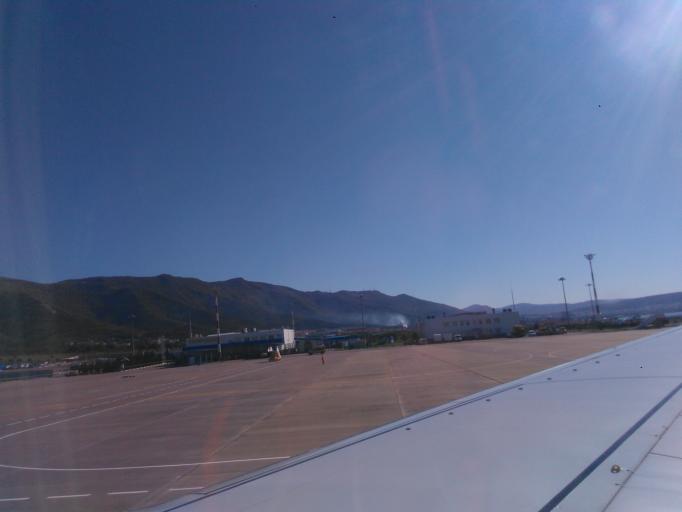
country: RU
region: Krasnodarskiy
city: Gelendzhik
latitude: 44.5938
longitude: 38.0223
